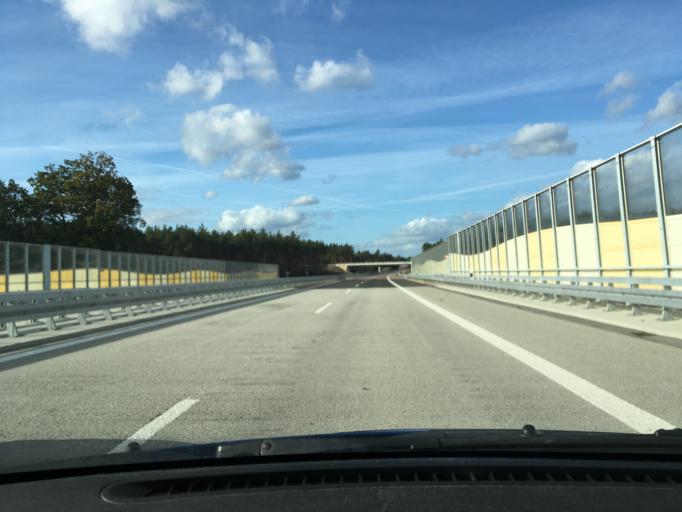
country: DE
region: Mecklenburg-Vorpommern
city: Grabow
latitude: 53.2600
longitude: 11.5362
